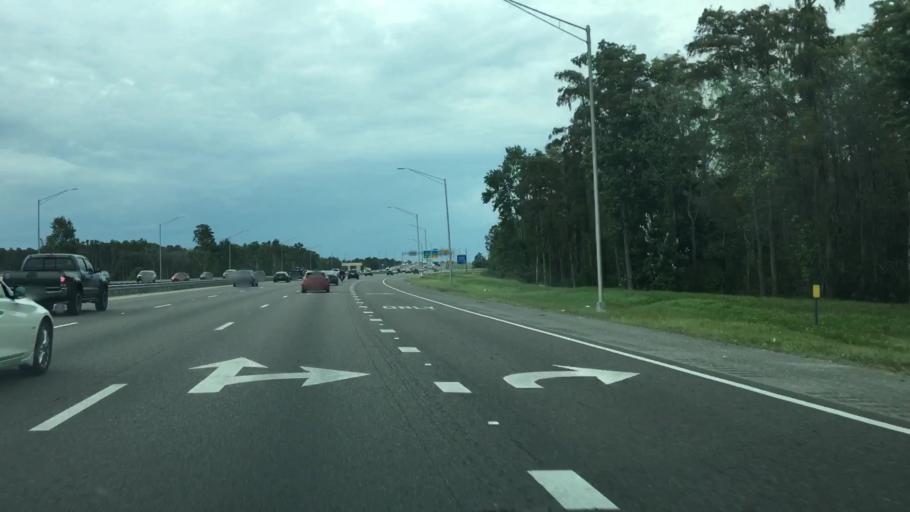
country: US
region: Florida
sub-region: Orange County
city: Azalea Park
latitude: 28.4697
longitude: -81.2371
